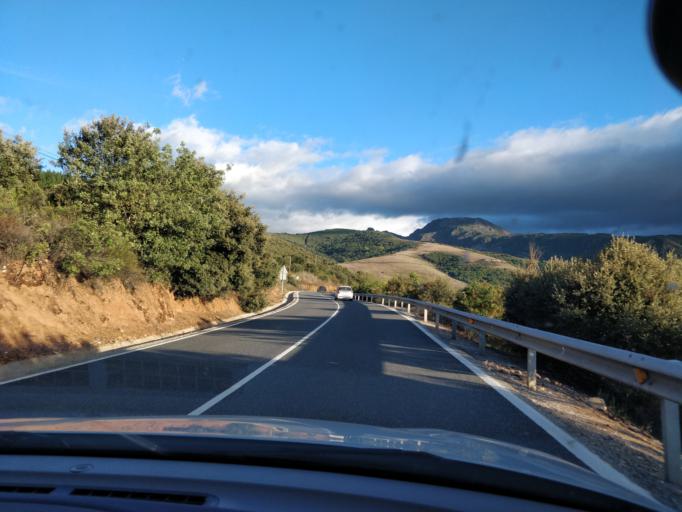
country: ES
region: Castille and Leon
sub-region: Provincia de Leon
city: Borrenes
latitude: 42.4965
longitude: -6.7187
